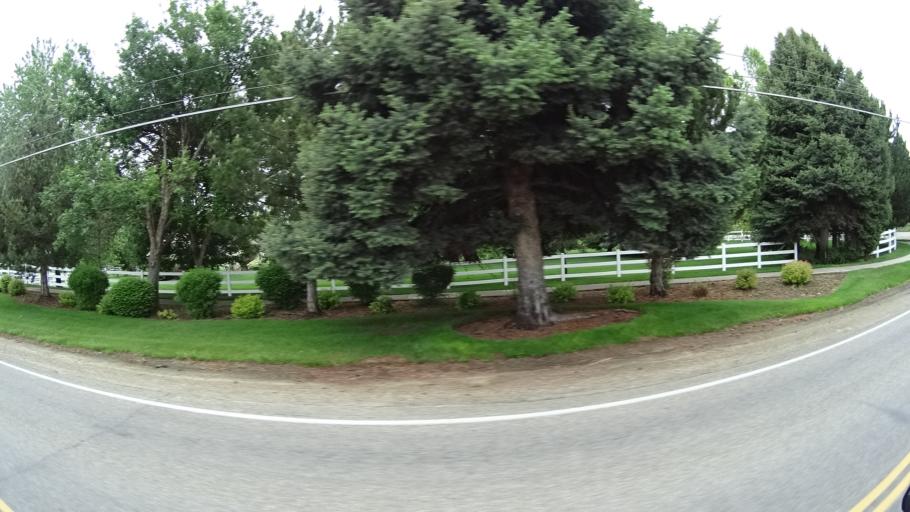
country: US
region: Idaho
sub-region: Ada County
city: Eagle
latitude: 43.7062
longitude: -116.3944
